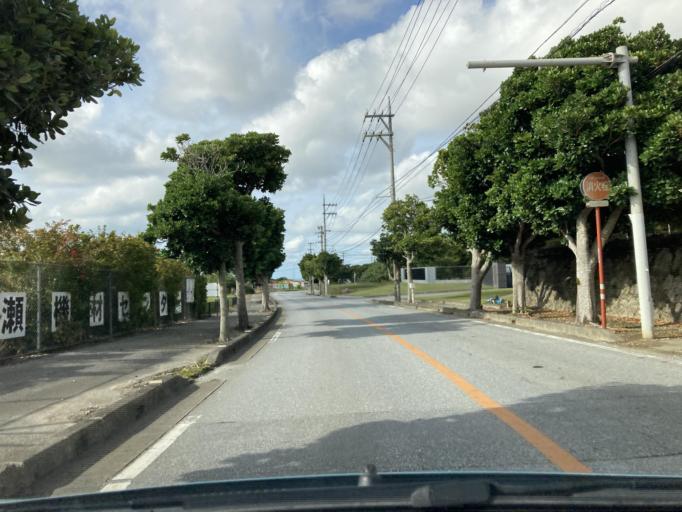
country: JP
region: Okinawa
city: Itoman
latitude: 26.1218
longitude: 127.7146
